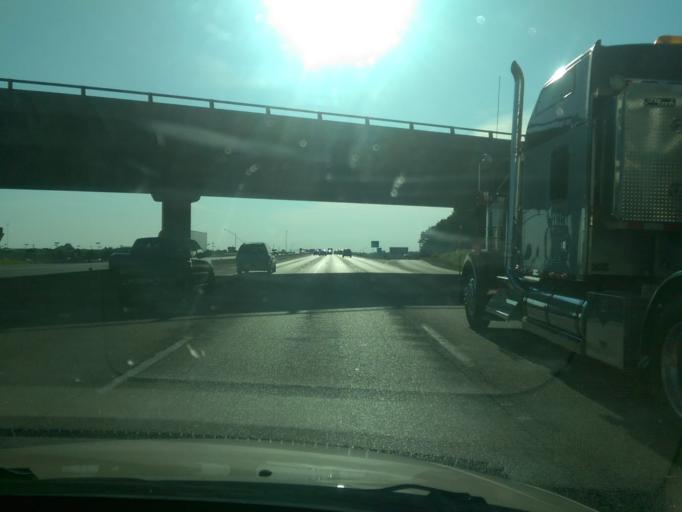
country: US
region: Missouri
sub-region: Jackson County
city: Raytown
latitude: 39.0471
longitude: -94.4393
